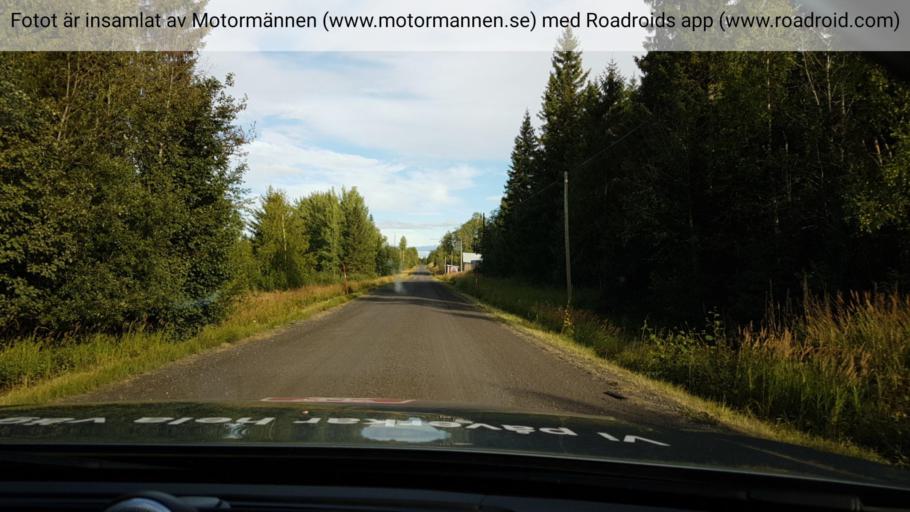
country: SE
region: Jaemtland
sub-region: Stroemsunds Kommun
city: Stroemsund
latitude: 64.1370
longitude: 15.7562
